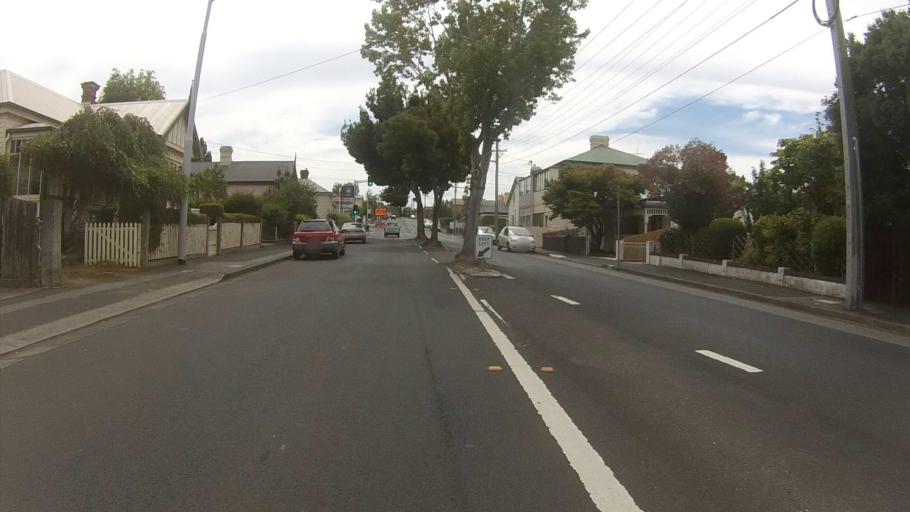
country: AU
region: Tasmania
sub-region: Hobart
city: Sandy Bay
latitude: -42.8981
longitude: 147.3240
